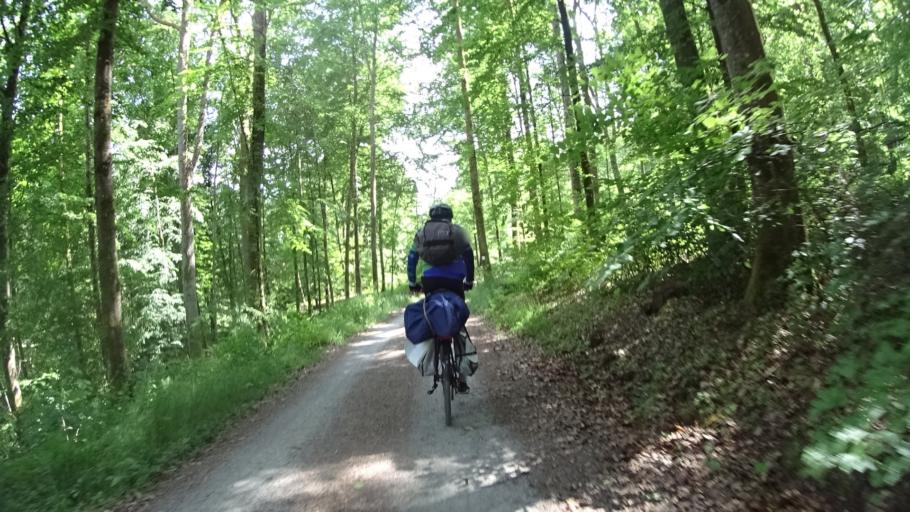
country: DE
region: Baden-Wuerttemberg
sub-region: Karlsruhe Region
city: Hopfingen
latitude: 49.6570
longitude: 9.4275
